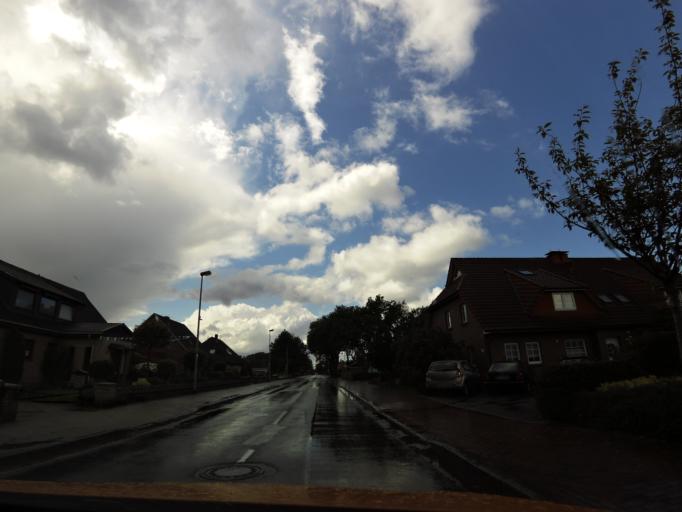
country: DE
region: Lower Saxony
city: Hatten
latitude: 53.1204
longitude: 8.3326
